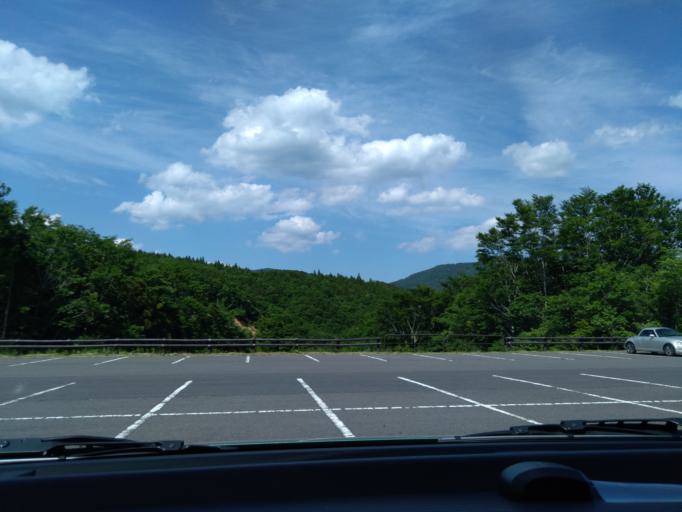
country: JP
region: Iwate
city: Ichinoseki
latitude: 39.0125
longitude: 140.8620
